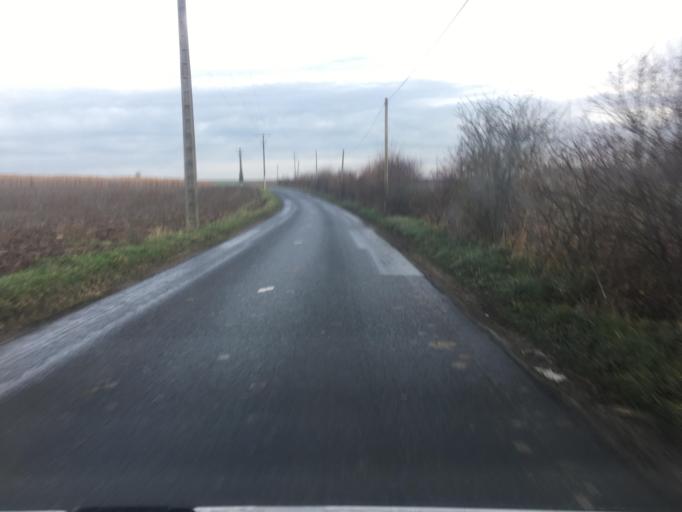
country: FR
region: Lower Normandy
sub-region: Departement du Calvados
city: Creully
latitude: 49.2568
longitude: -0.5625
